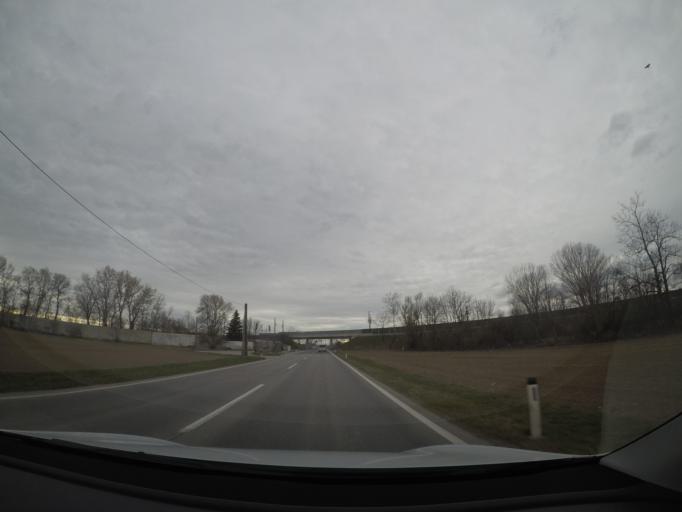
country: AT
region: Lower Austria
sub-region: Politischer Bezirk Modling
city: Achau
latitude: 48.0744
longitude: 16.3863
